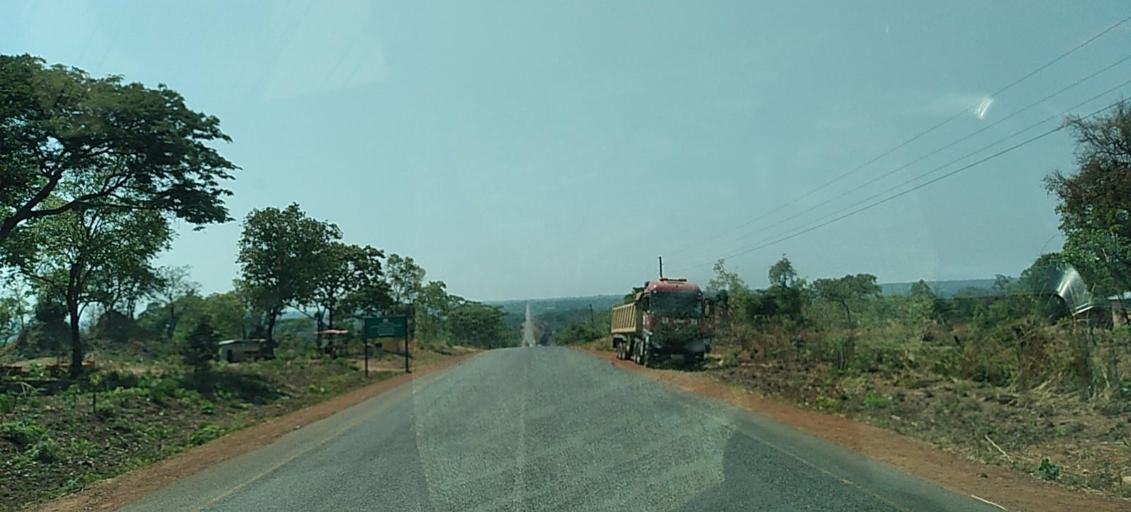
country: ZM
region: North-Western
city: Solwezi
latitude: -12.3317
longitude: 25.8921
